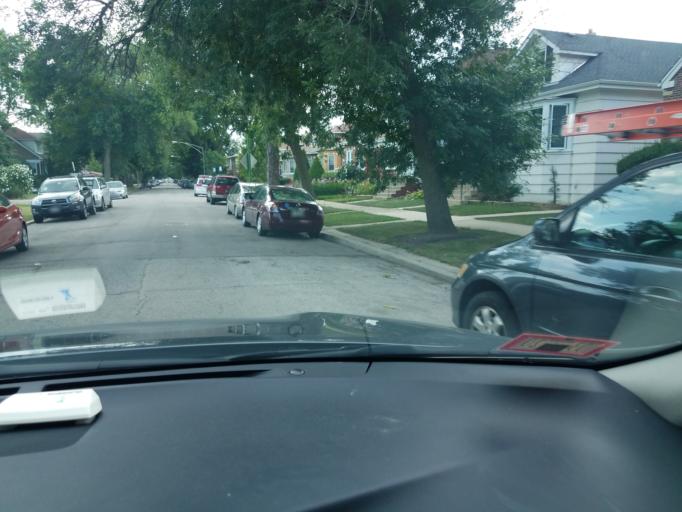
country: US
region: Illinois
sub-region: Cook County
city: Harwood Heights
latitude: 41.9866
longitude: -87.7719
